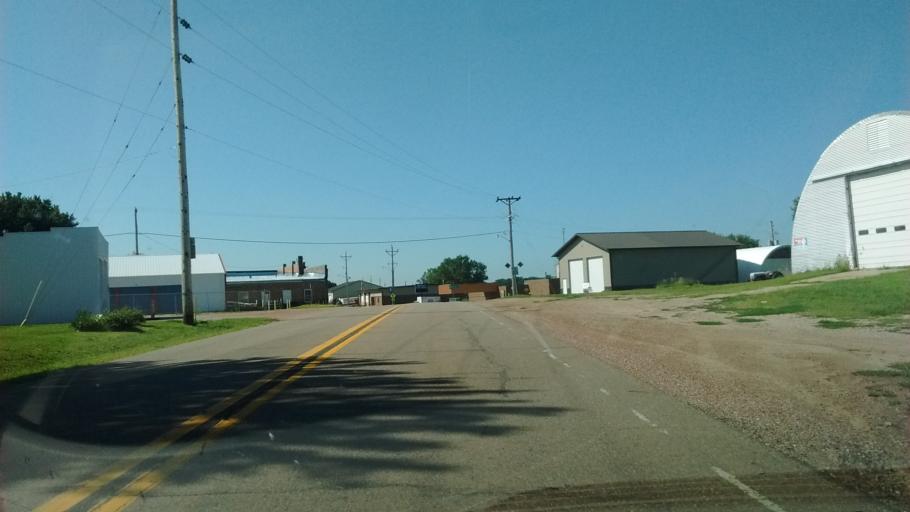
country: US
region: Iowa
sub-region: Woodbury County
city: Moville
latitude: 42.4902
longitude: -96.0747
